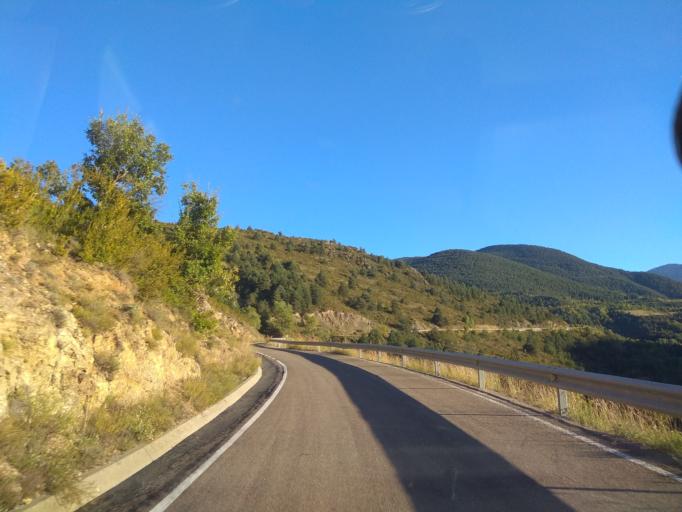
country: ES
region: Catalonia
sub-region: Provincia de Lleida
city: Lles de Cerdanya
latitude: 42.3558
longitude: 1.6882
